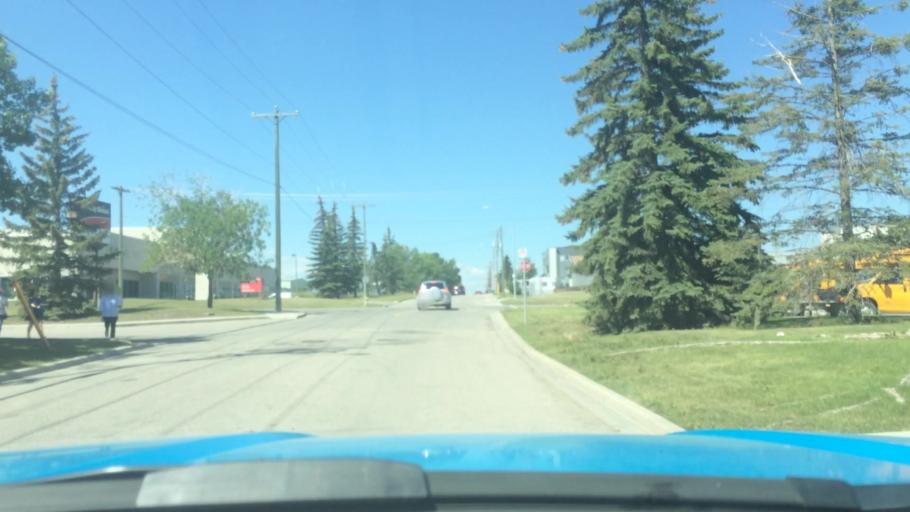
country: CA
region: Alberta
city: Calgary
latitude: 51.0545
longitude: -113.9924
